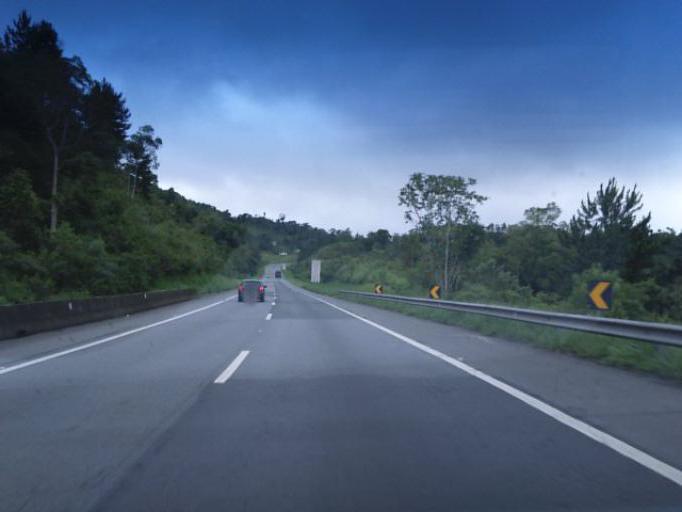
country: BR
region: Parana
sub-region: Antonina
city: Antonina
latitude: -25.0537
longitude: -48.5516
